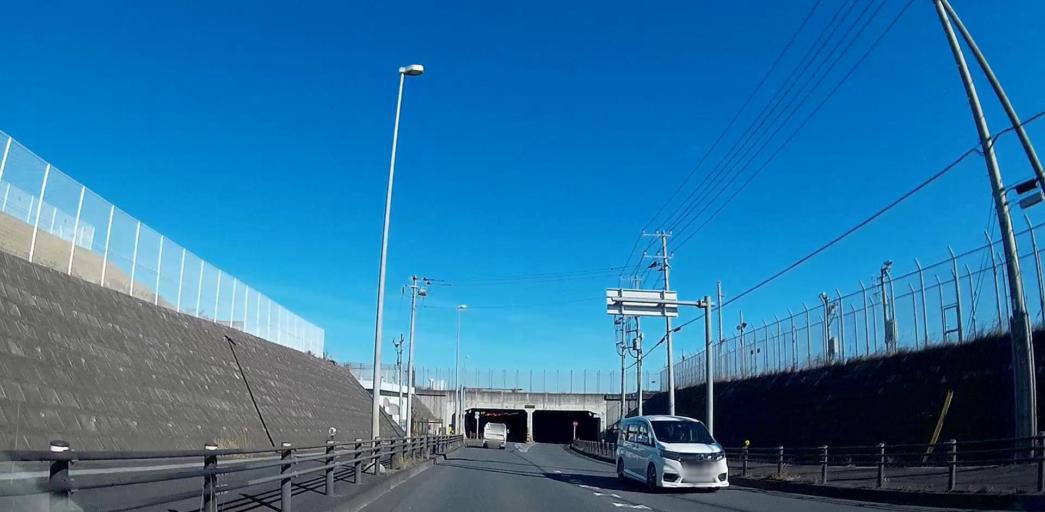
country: JP
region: Chiba
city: Narita
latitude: 35.8020
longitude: 140.3761
